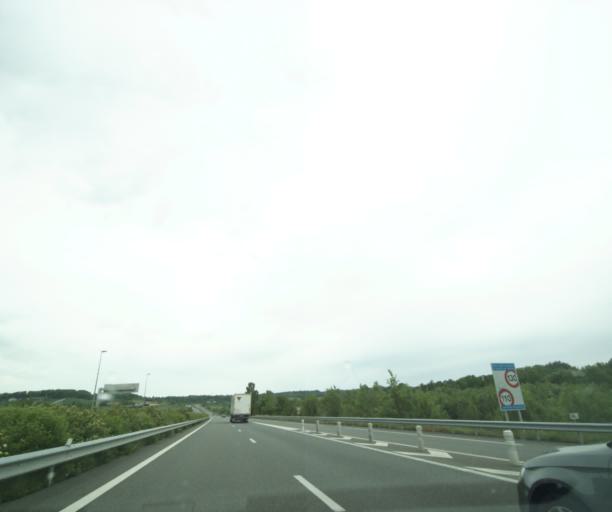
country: FR
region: Midi-Pyrenees
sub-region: Departement du Tarn-et-Garonne
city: Caussade
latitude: 44.2373
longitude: 1.5256
